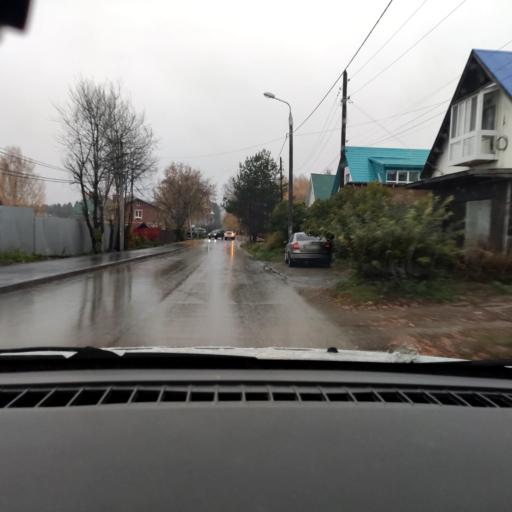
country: RU
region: Perm
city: Kondratovo
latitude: 58.0451
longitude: 56.1070
